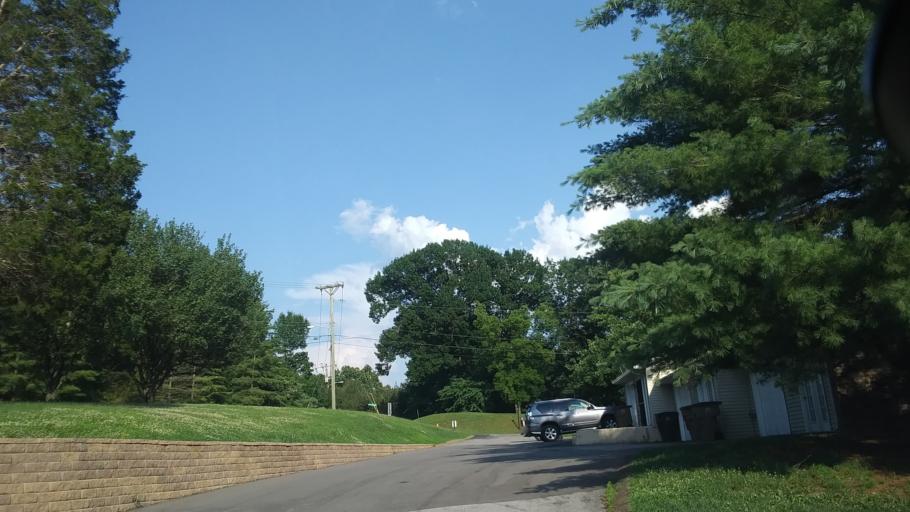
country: US
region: Tennessee
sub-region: Rutherford County
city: La Vergne
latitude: 36.0755
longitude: -86.6644
